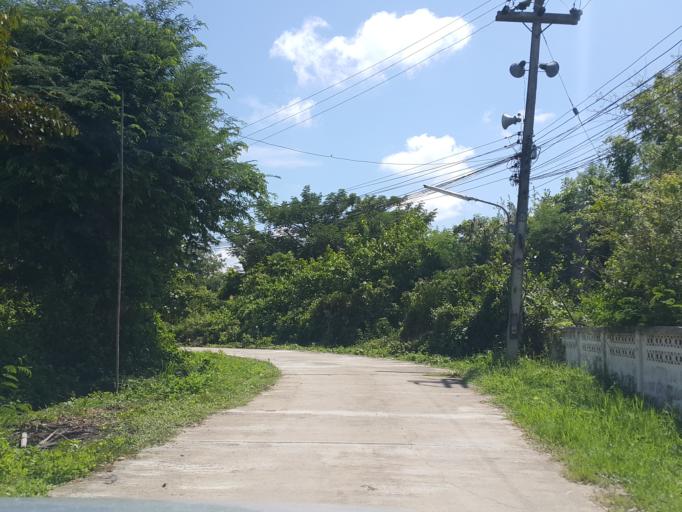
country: TH
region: Chiang Mai
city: San Kamphaeng
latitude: 18.7153
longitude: 99.1096
